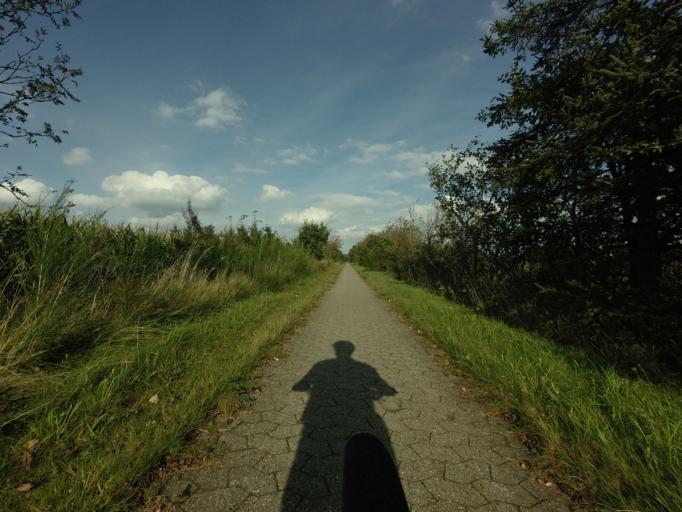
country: DK
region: Central Jutland
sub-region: Viborg Kommune
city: Karup
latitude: 56.3294
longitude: 9.2282
